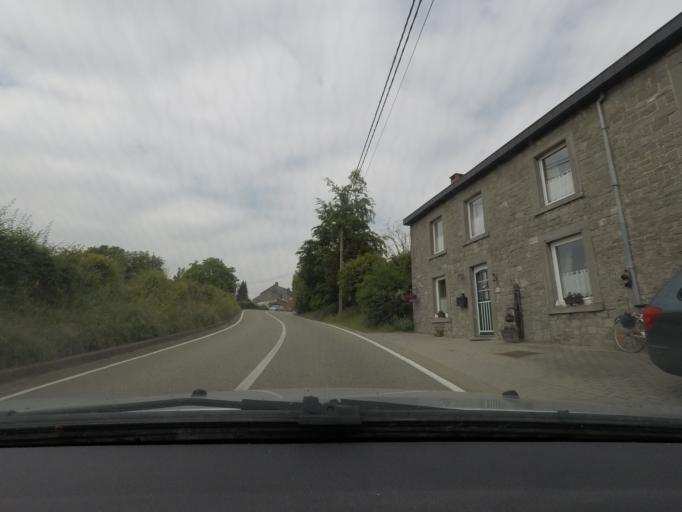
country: BE
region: Wallonia
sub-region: Province de Namur
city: Noville-les-Bois
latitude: 50.4750
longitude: 4.9977
